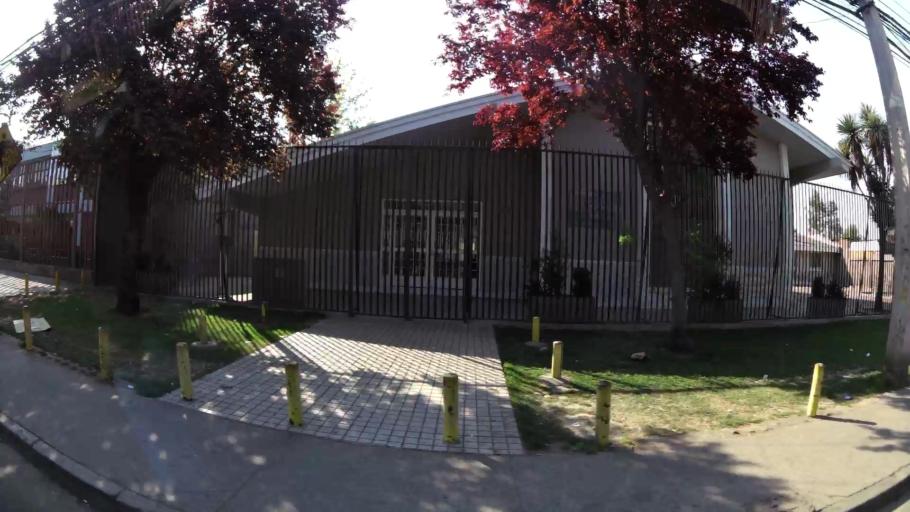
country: CL
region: Santiago Metropolitan
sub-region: Provincia de Santiago
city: Lo Prado
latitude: -33.3845
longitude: -70.6794
